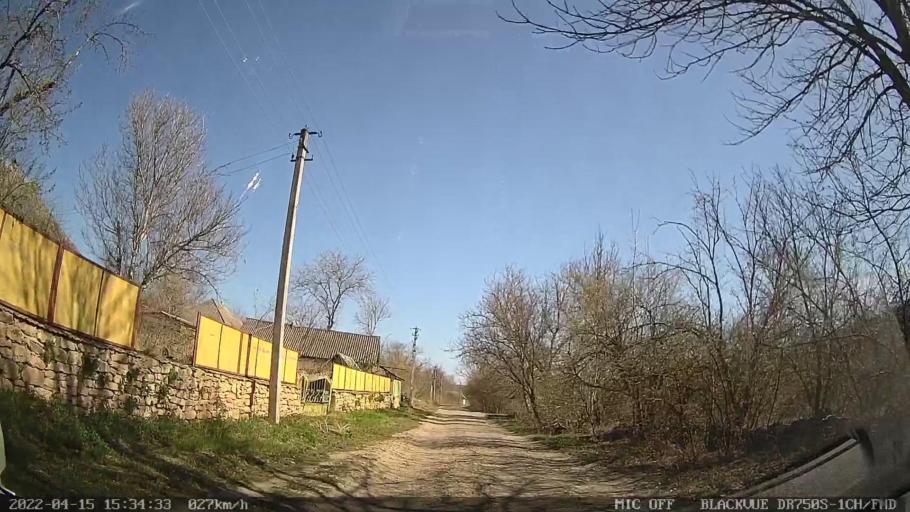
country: MD
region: Raionul Ocnita
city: Otaci
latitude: 48.3471
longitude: 27.9278
